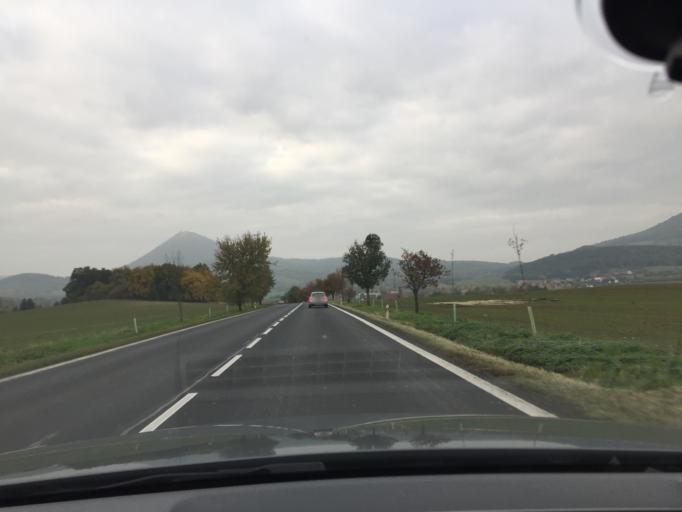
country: CZ
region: Ustecky
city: Velemin
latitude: 50.5335
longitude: 13.9851
